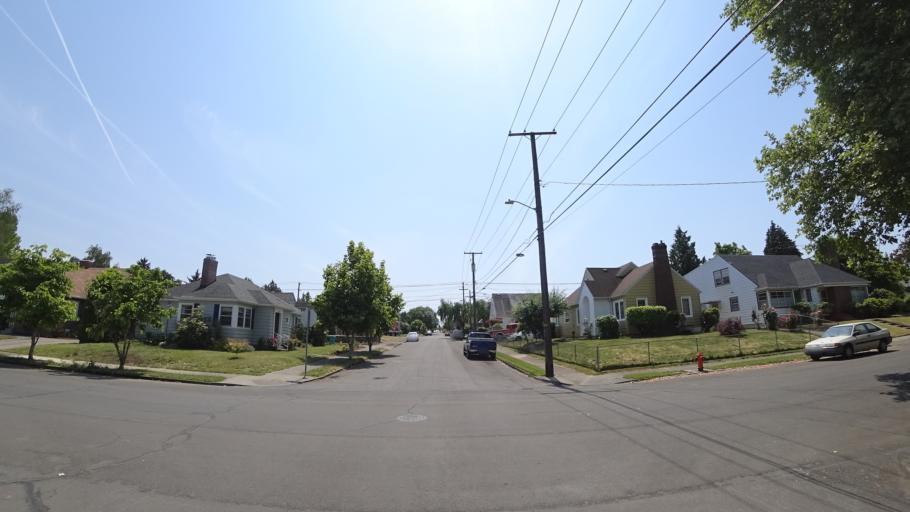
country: US
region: Oregon
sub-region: Multnomah County
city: Portland
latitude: 45.5780
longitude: -122.6707
